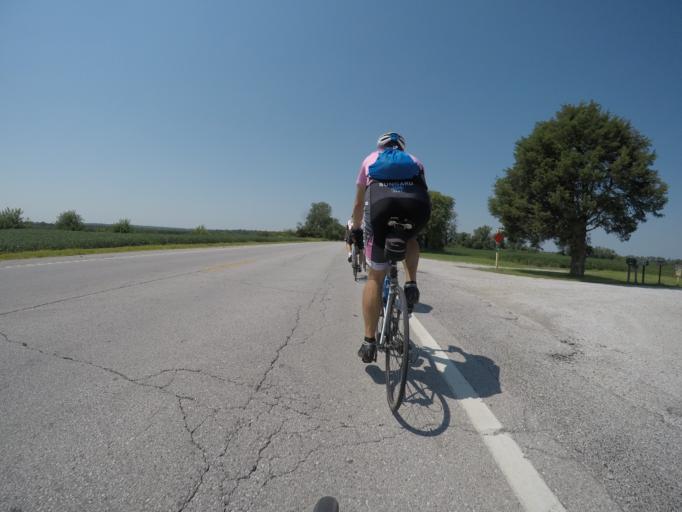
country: US
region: Kansas
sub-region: Leavenworth County
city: Leavenworth
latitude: 39.3265
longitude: -94.8732
